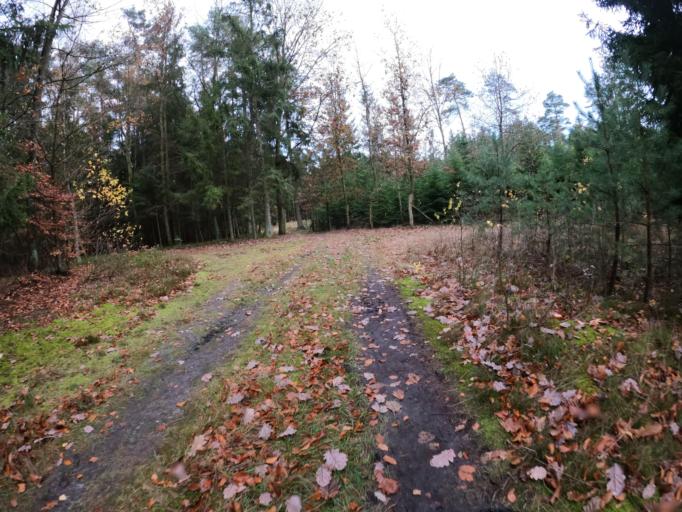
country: PL
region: West Pomeranian Voivodeship
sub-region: Powiat walecki
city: Tuczno
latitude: 53.2246
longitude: 16.2667
